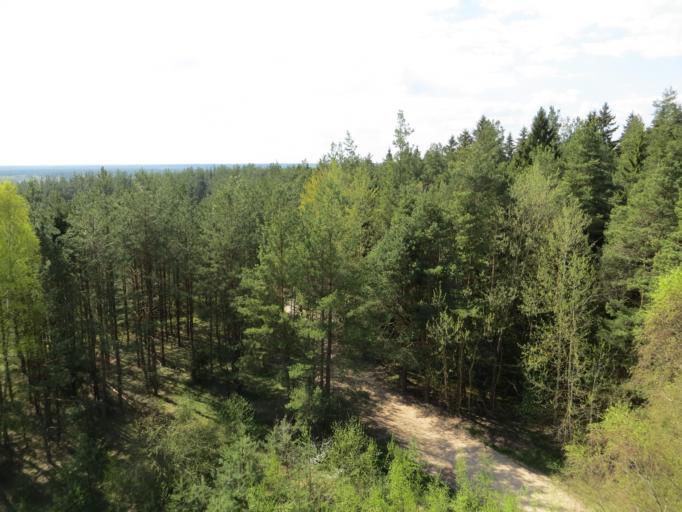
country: LT
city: Svencioneliai
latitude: 55.1745
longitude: 26.0125
